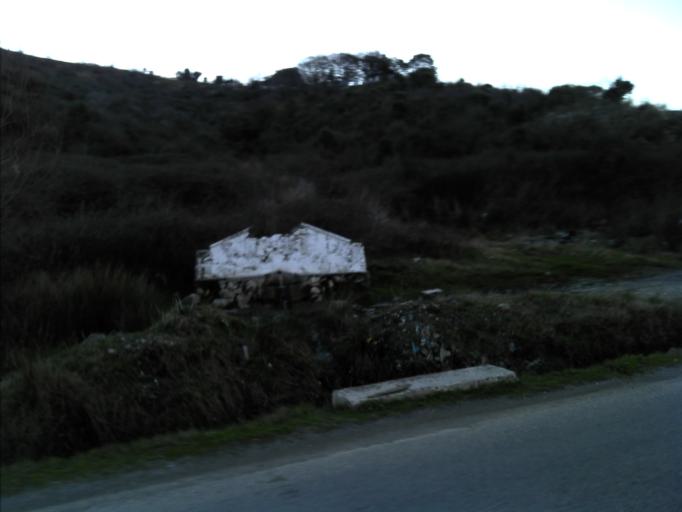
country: AL
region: Shkoder
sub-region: Rrethi i Shkodres
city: Berdica e Madhe
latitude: 42.0198
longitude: 19.4850
